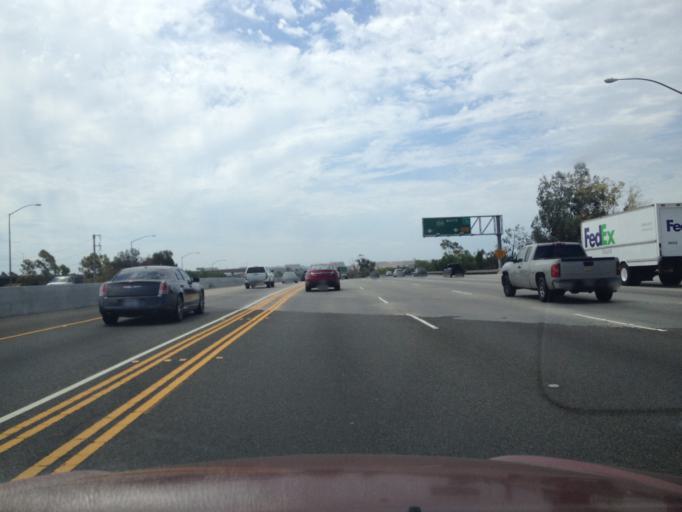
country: US
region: California
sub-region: Orange County
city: Irvine
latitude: 33.6737
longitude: -117.7561
